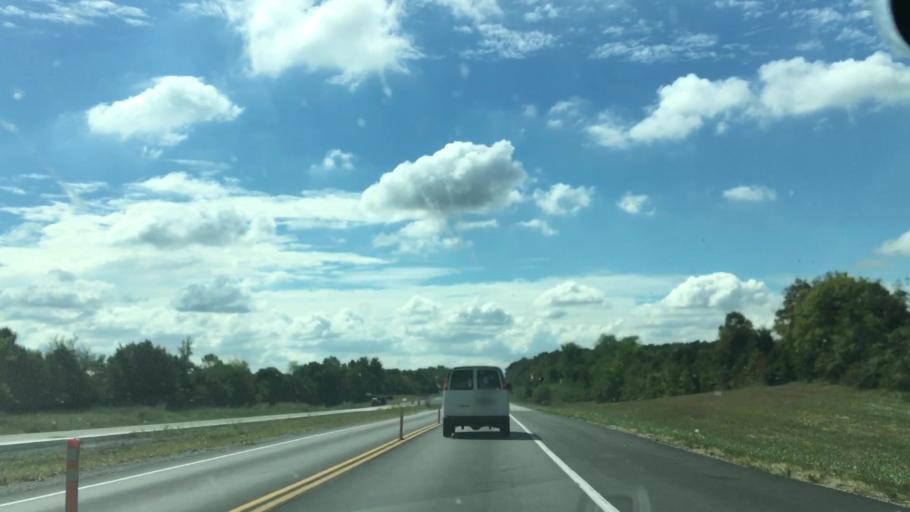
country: US
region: Kentucky
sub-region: Christian County
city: Hopkinsville
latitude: 36.9657
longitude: -87.4661
